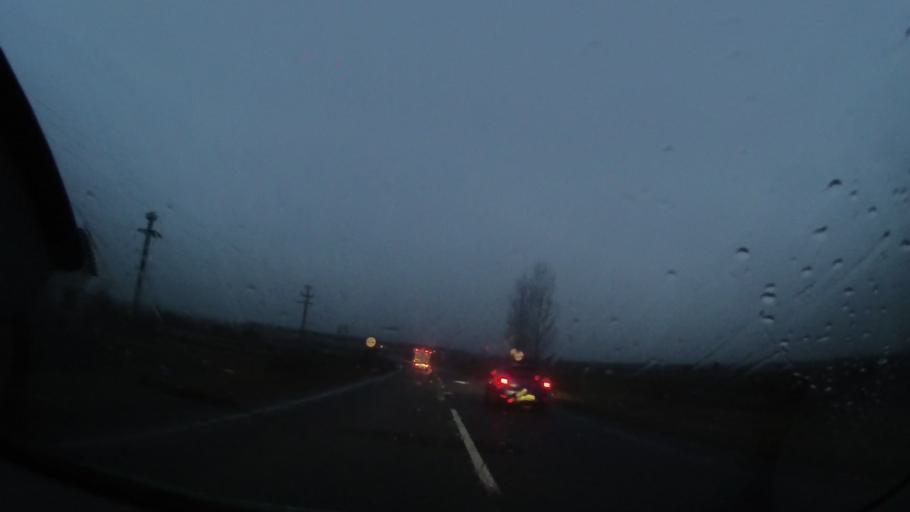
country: RO
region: Harghita
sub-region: Comuna Ditrau
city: Ditrau
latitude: 46.8170
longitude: 25.4924
